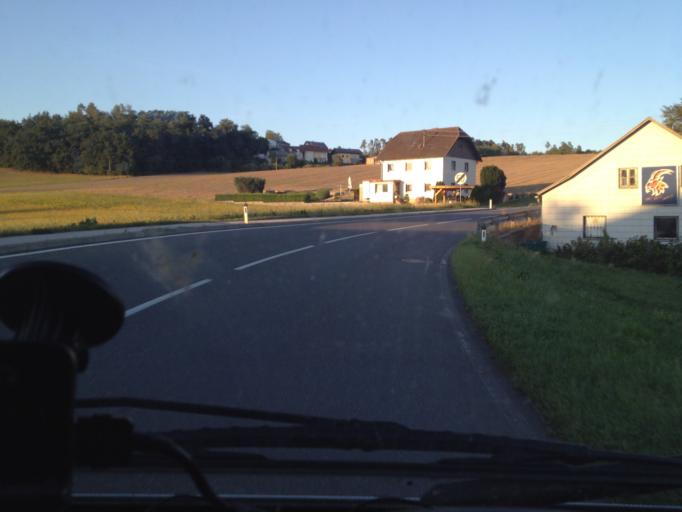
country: AT
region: Upper Austria
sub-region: Politischer Bezirk Urfahr-Umgebung
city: Gallneukirchen
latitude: 48.3554
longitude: 14.4300
